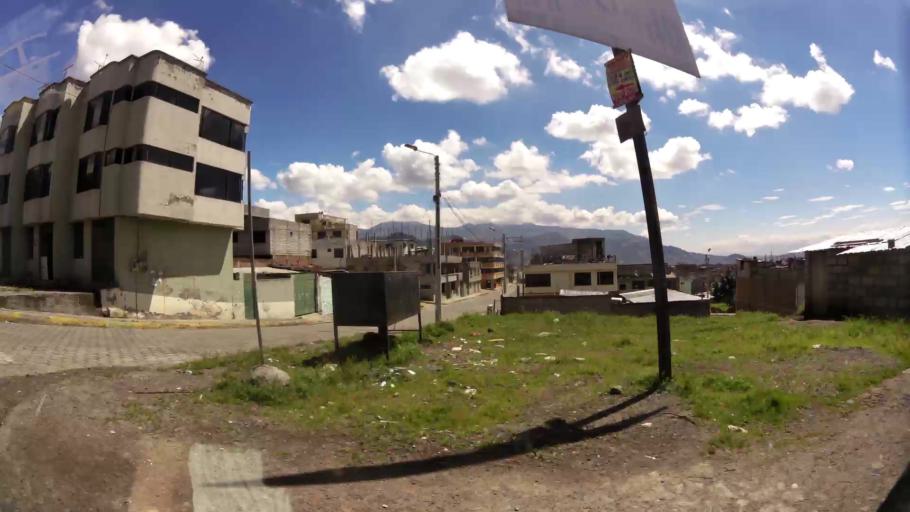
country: EC
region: Pichincha
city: Quito
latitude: -0.3157
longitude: -78.5617
